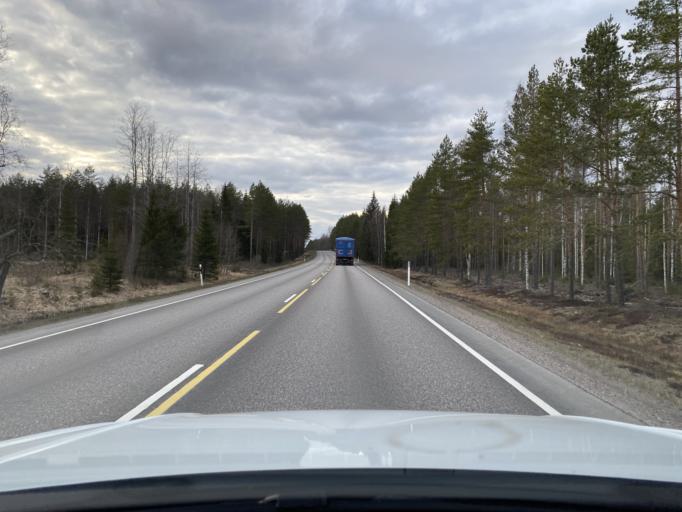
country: FI
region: Uusimaa
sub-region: Helsinki
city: Kaerkoelae
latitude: 60.8169
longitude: 24.0440
